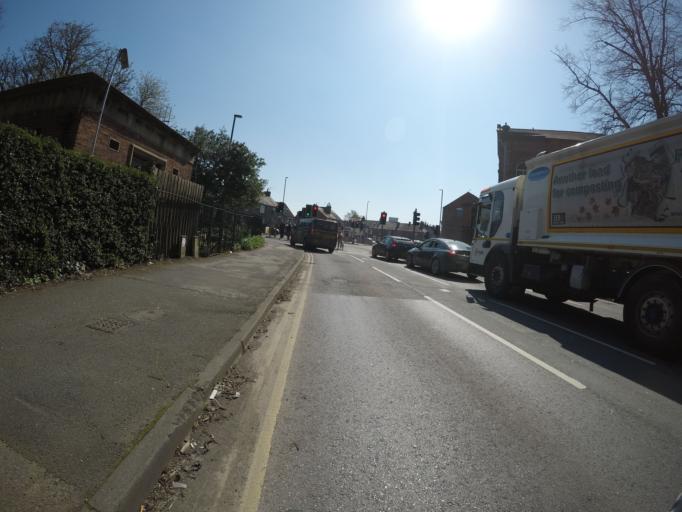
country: GB
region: England
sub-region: City of York
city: York
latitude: 53.9684
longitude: -1.0814
